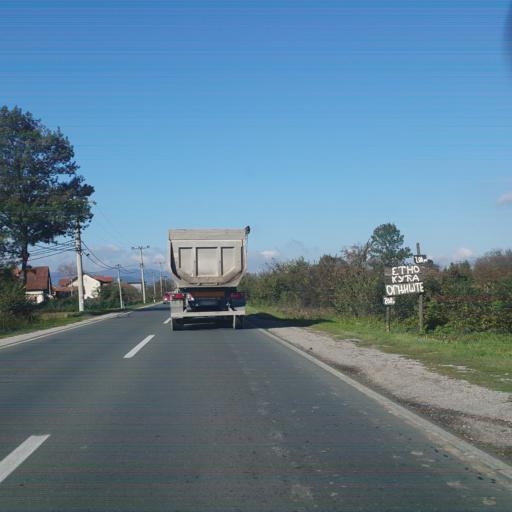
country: RS
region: Central Serbia
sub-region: Rasinski Okrug
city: Trstenik
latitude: 43.6329
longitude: 20.9583
